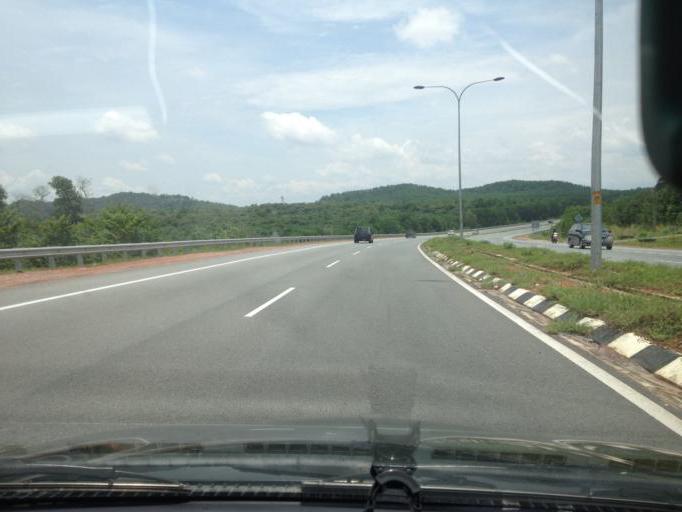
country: MY
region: Kedah
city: Sungai Petani
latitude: 5.6181
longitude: 100.5530
